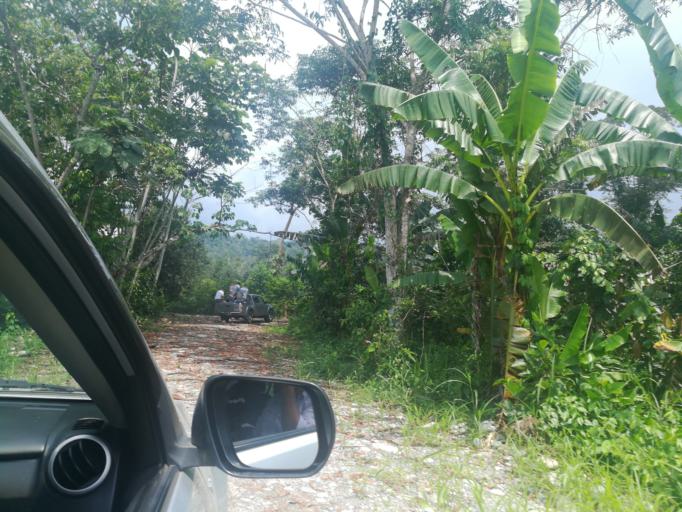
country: EC
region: Napo
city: Tena
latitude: -1.0302
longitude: -77.6788
